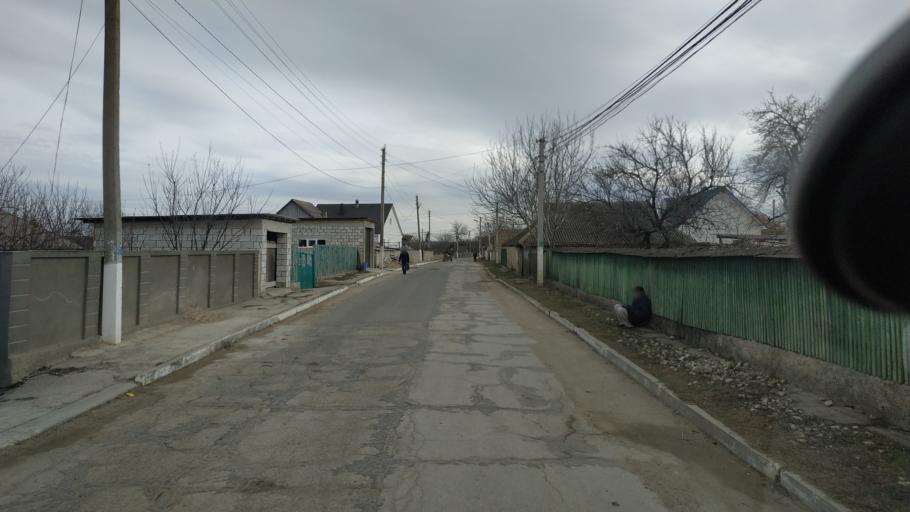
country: MD
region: Telenesti
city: Cocieri
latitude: 47.3824
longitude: 29.1173
